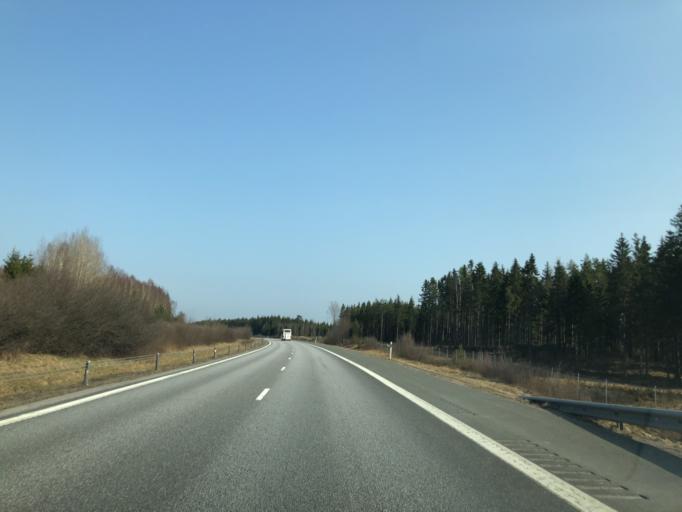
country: SE
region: Joenkoeping
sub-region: Varnamo Kommun
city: Varnamo
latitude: 57.2122
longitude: 14.0840
